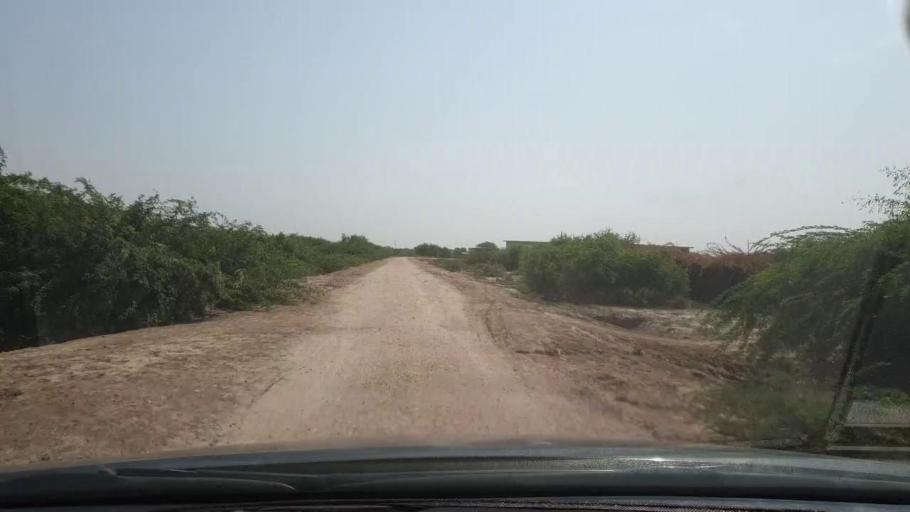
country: PK
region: Sindh
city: Naukot
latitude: 24.8076
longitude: 69.2441
